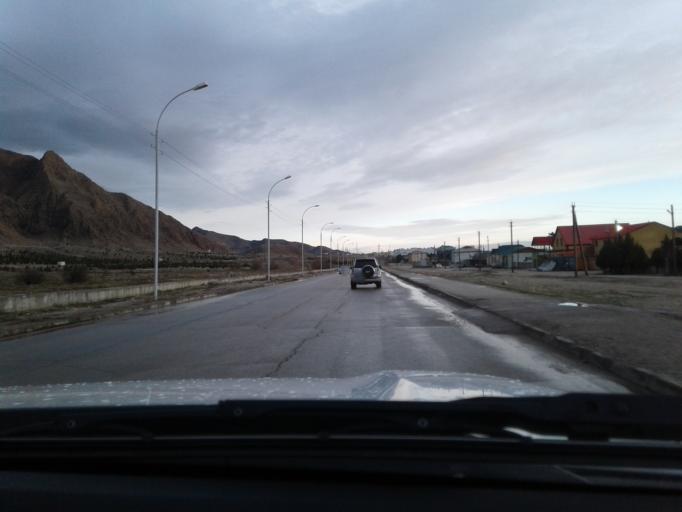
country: TM
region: Balkan
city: Balkanabat
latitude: 39.5302
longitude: 54.3567
